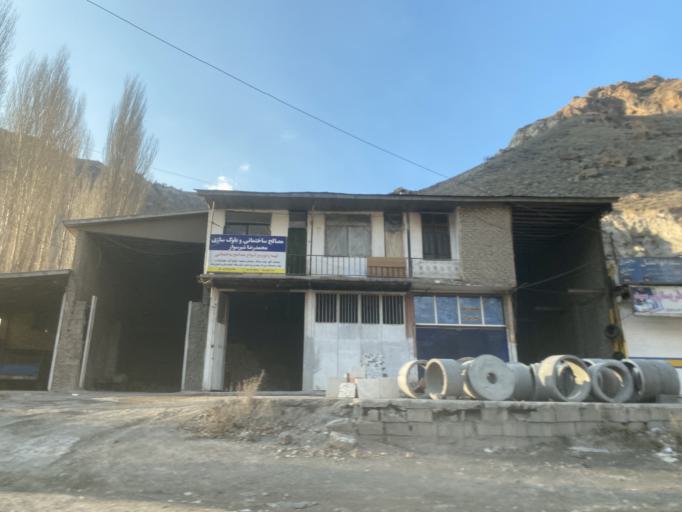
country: IR
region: Tehran
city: Damavand
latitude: 35.8932
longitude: 52.2080
